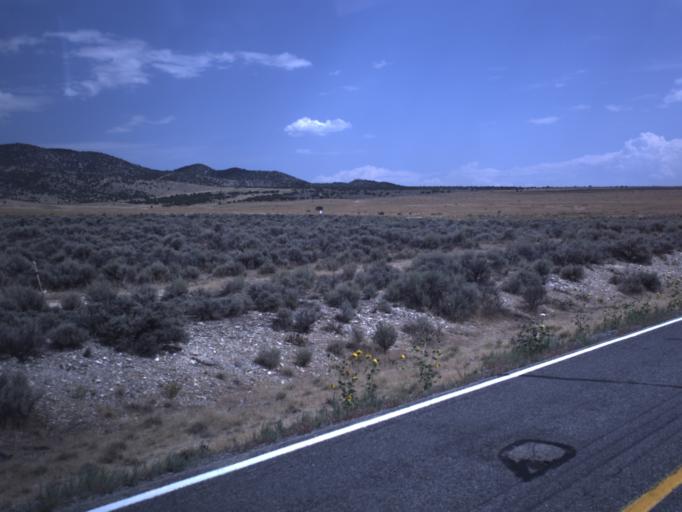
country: US
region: Utah
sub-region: Utah County
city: Eagle Mountain
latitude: 40.2747
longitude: -112.2498
